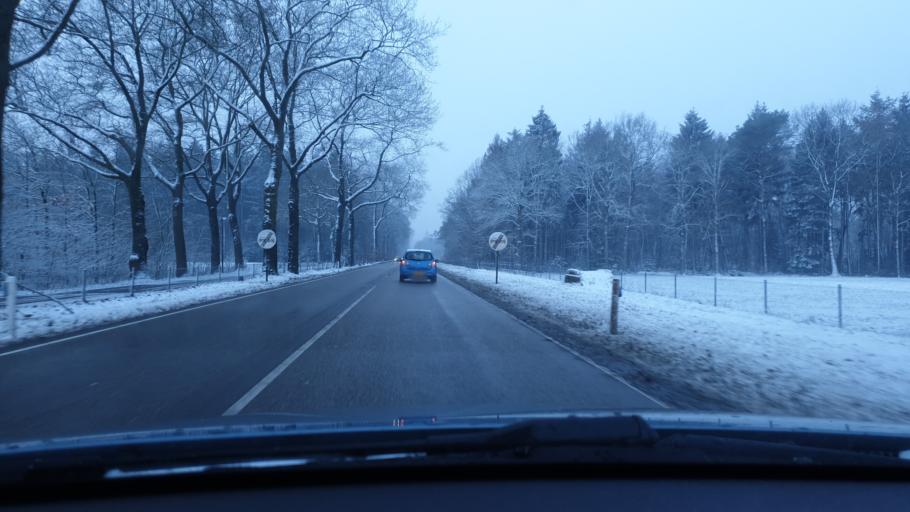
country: NL
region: North Brabant
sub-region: Gemeente Landerd
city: Zeeland
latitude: 51.6860
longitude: 5.6582
